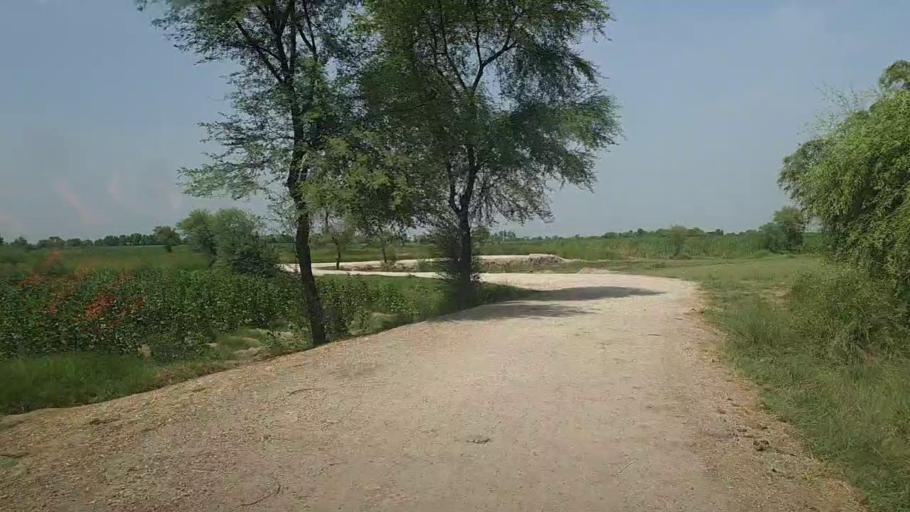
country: PK
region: Sindh
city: Ubauro
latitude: 28.1594
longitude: 69.8276
